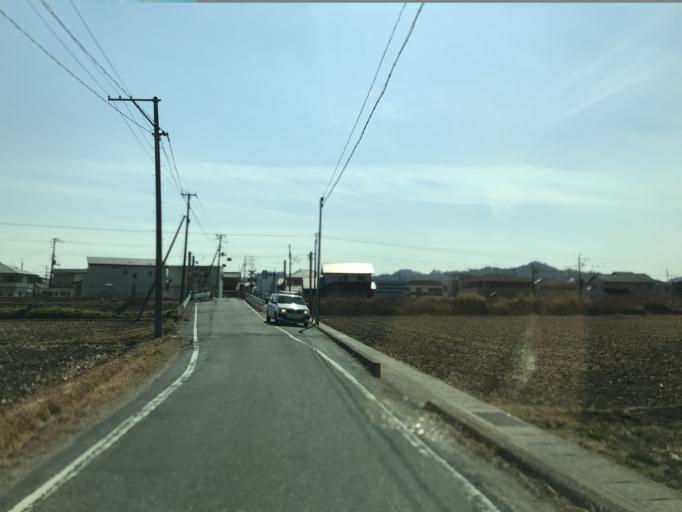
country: JP
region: Fukushima
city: Iwaki
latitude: 37.0663
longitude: 140.9317
